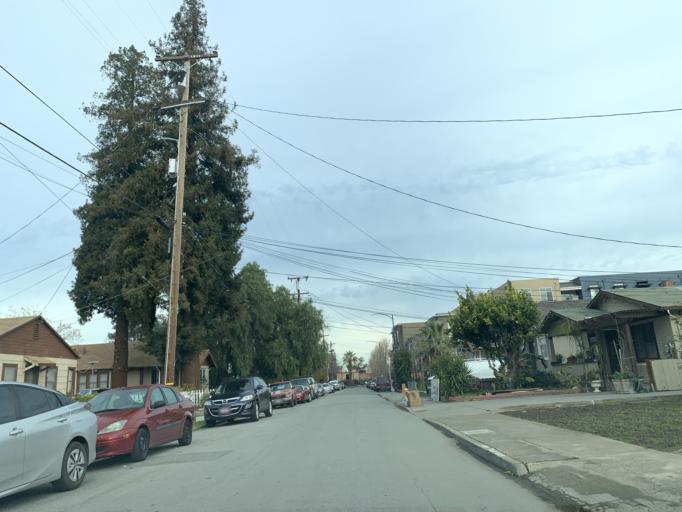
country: US
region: California
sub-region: Santa Clara County
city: Buena Vista
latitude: 37.3218
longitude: -121.9155
